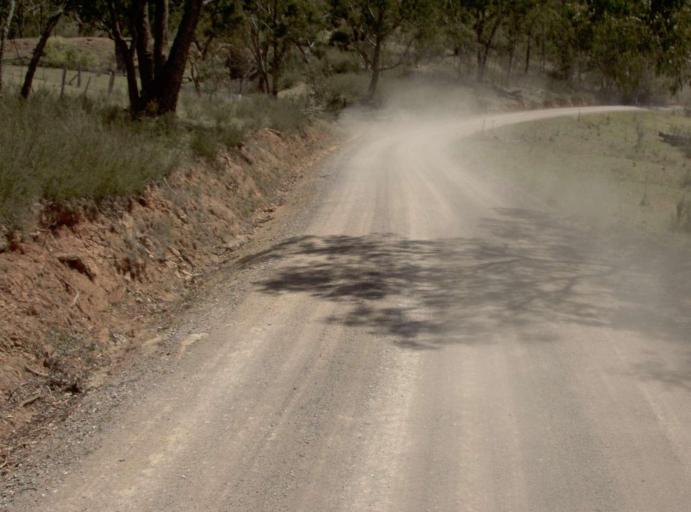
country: AU
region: New South Wales
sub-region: Snowy River
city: Jindabyne
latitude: -37.0399
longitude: 148.5570
